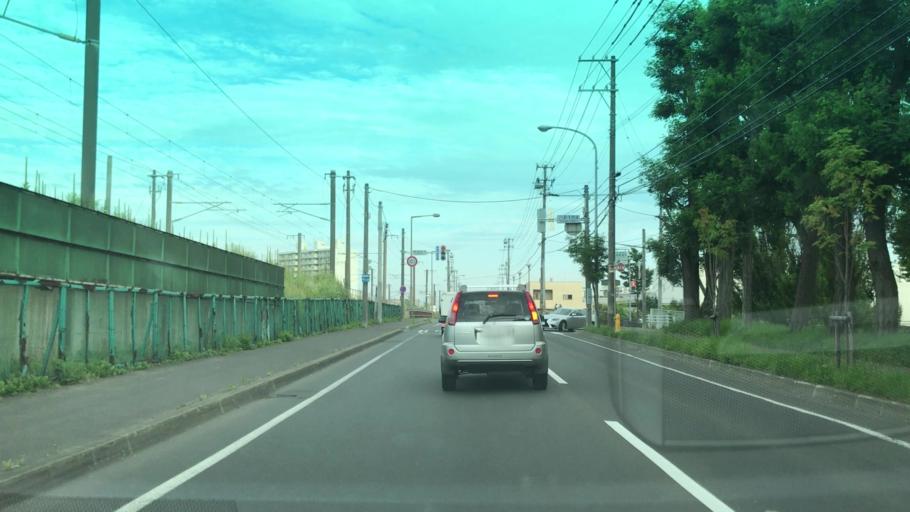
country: JP
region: Hokkaido
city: Sapporo
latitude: 43.0842
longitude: 141.3033
